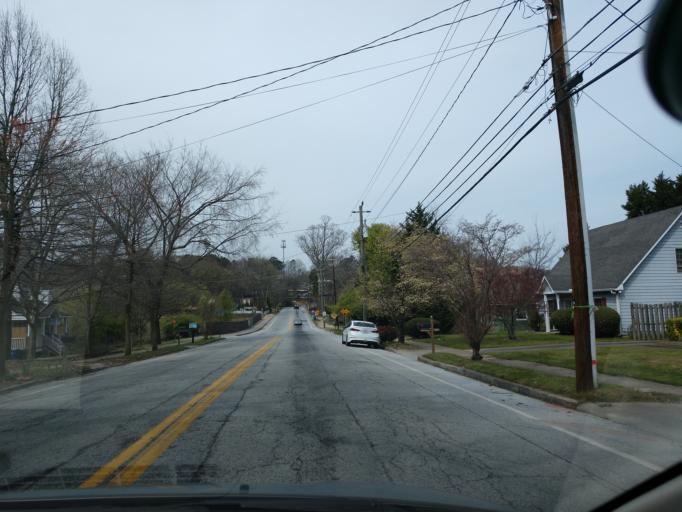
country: US
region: Georgia
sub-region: Fulton County
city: Atlanta
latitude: 33.7270
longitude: -84.3600
